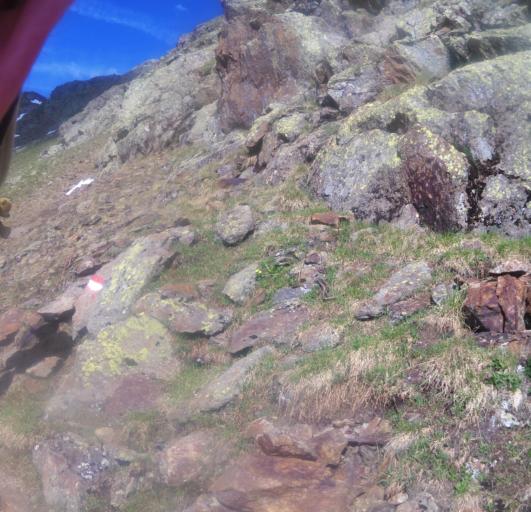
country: AT
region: Tyrol
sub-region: Politischer Bezirk Innsbruck Land
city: Gschnitz
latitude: 46.9898
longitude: 11.2487
